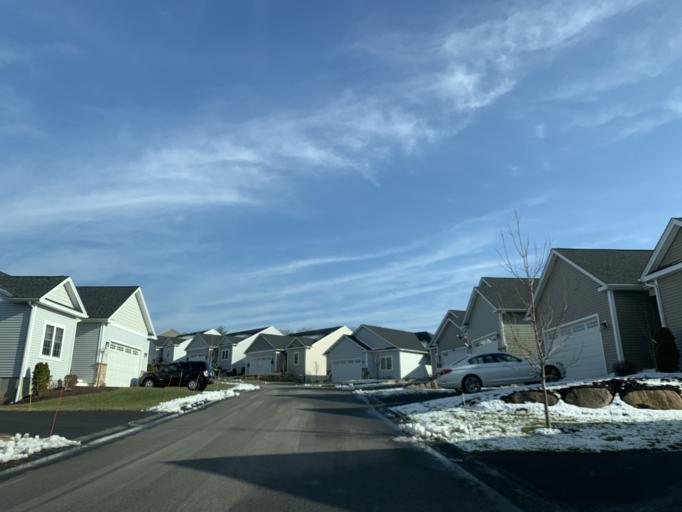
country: US
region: Rhode Island
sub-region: Kent County
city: West Warwick
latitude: 41.6560
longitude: -71.5495
